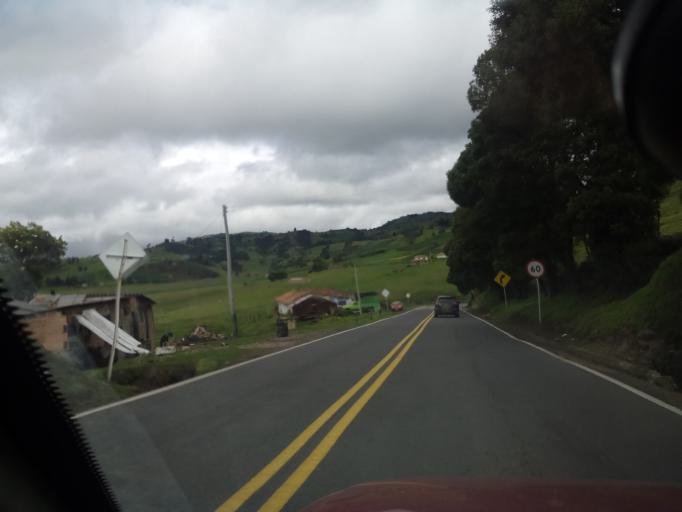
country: CO
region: Boyaca
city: Combita
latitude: 5.6645
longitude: -73.3608
